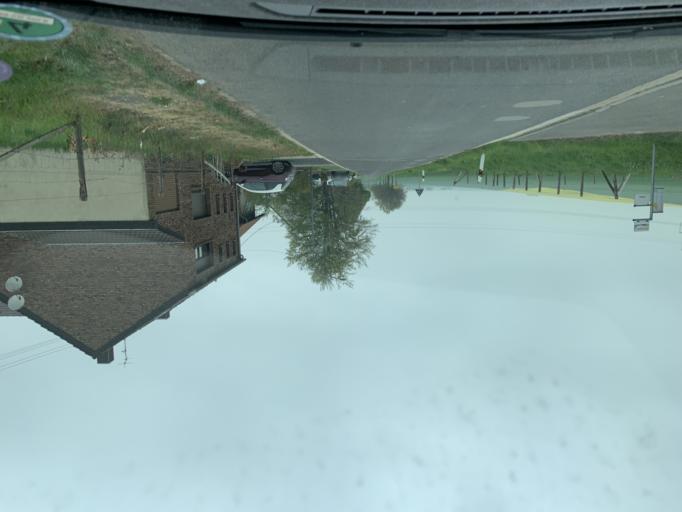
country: DE
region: North Rhine-Westphalia
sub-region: Regierungsbezirk Koln
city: Vettweiss
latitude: 50.6883
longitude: 6.5549
